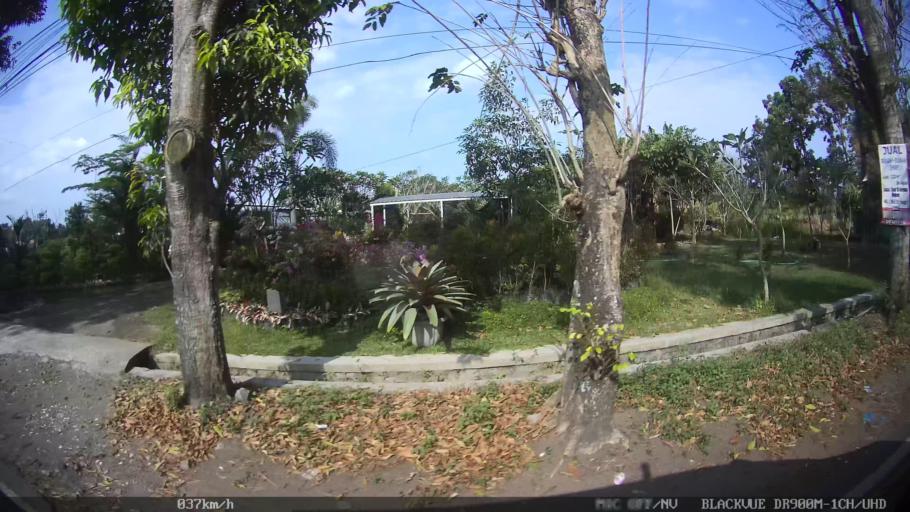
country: ID
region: Daerah Istimewa Yogyakarta
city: Depok
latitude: -7.7301
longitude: 110.4350
